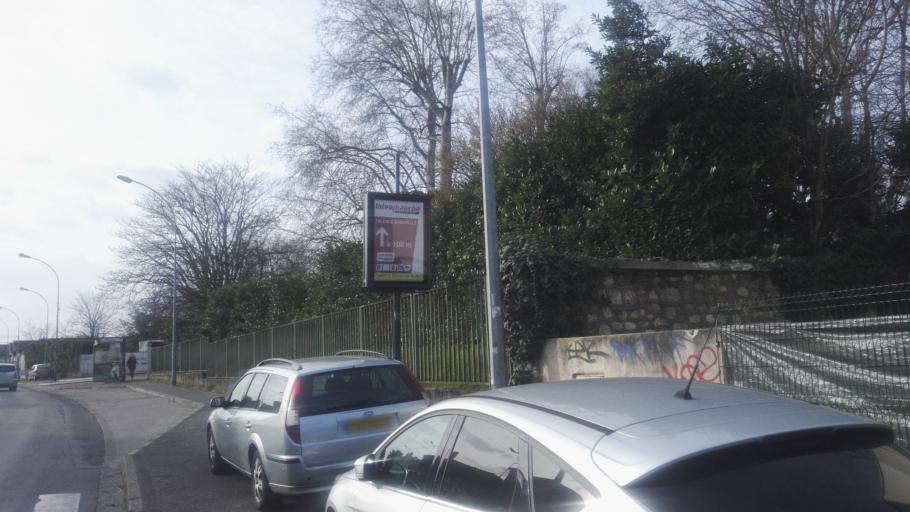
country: FR
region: Aquitaine
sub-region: Departement de la Gironde
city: Talence
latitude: 44.8090
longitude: -0.5740
